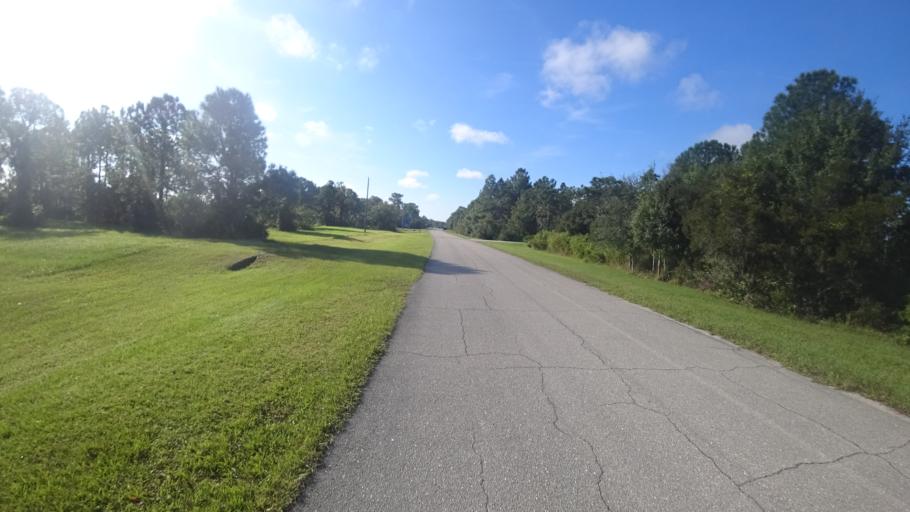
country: US
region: Florida
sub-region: Sarasota County
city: The Meadows
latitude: 27.4220
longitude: -82.3327
